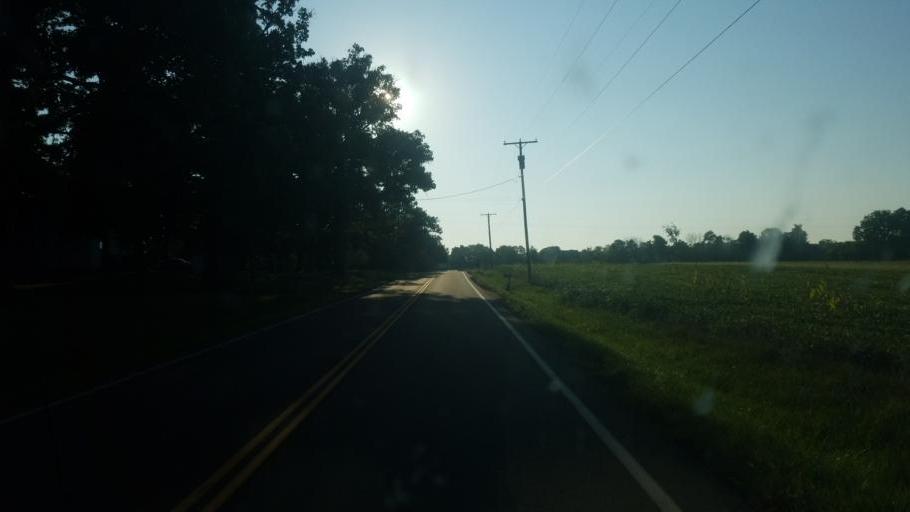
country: US
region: Ohio
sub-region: Richland County
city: Lincoln Heights
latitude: 40.8941
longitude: -82.5007
